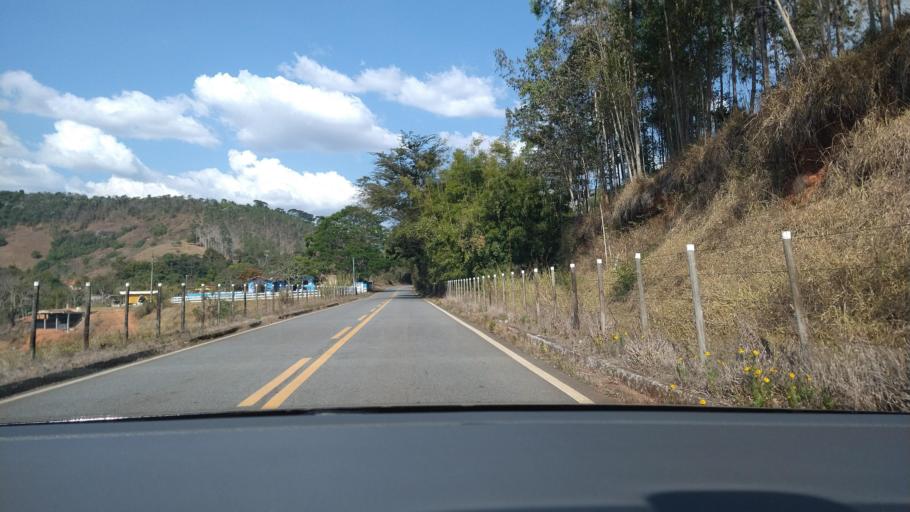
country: BR
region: Minas Gerais
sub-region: Rio Piracicaba
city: Rio Piracicaba
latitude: -19.9566
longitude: -43.1598
